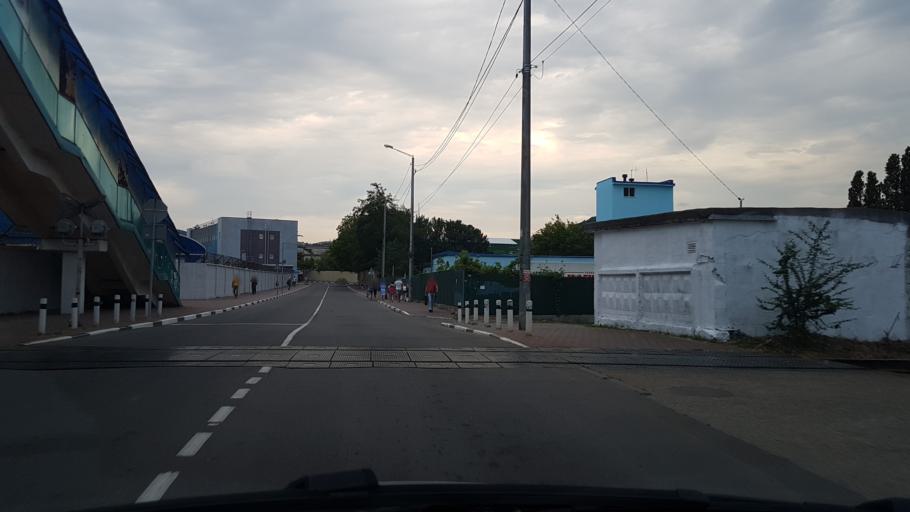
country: RU
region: Krasnodarskiy
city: Tuapse
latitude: 44.0923
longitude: 39.0804
